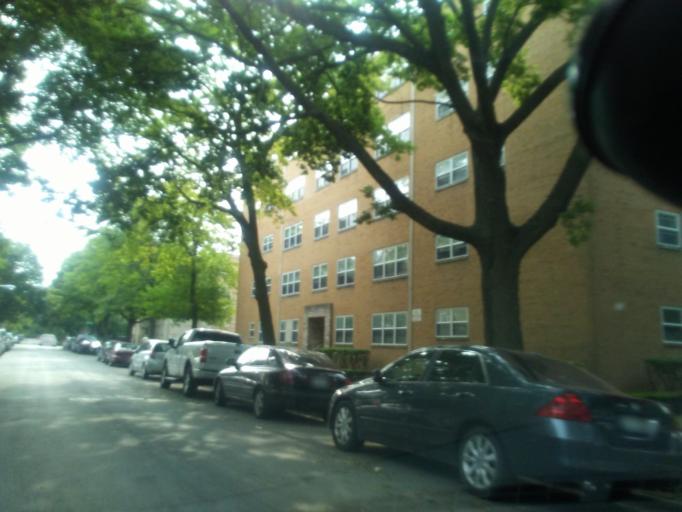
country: US
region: Illinois
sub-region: Cook County
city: Evanston
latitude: 41.9931
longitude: -87.6798
